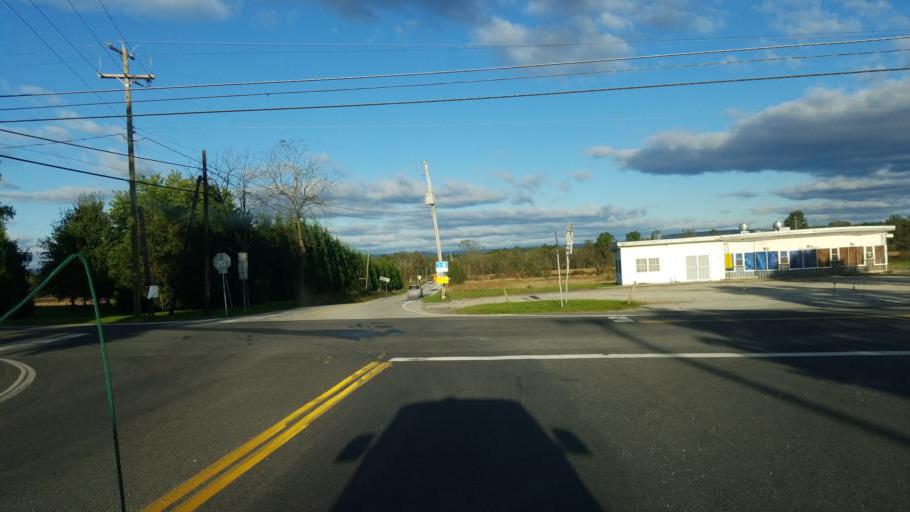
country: US
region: Pennsylvania
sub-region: Adams County
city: Biglerville
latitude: 39.8925
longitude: -77.1895
